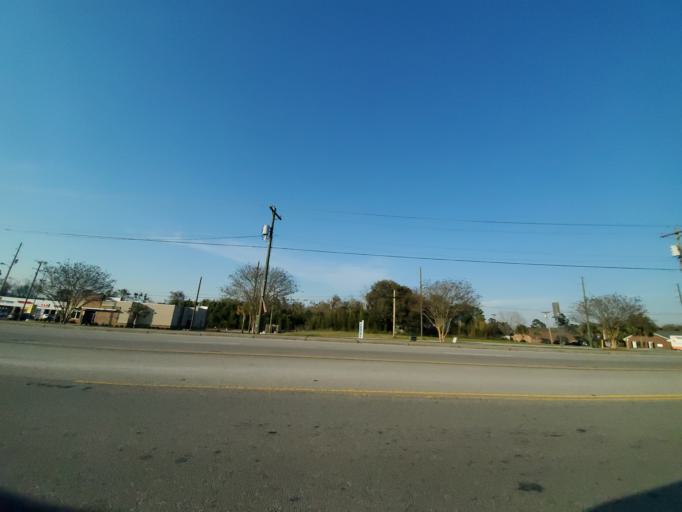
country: US
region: South Carolina
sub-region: Bamberg County
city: Bamberg
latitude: 33.2974
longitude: -81.0363
